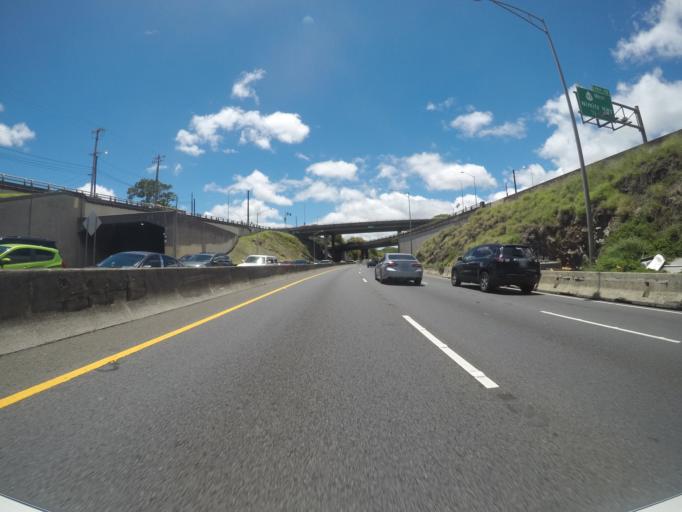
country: US
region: Hawaii
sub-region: Honolulu County
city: Honolulu
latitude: 21.3371
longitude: -157.8830
